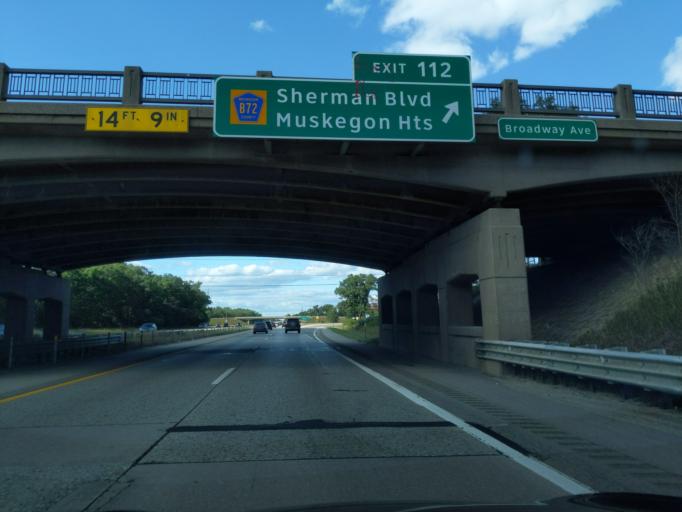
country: US
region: Michigan
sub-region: Muskegon County
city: Muskegon Heights
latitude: 43.2008
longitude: -86.2049
